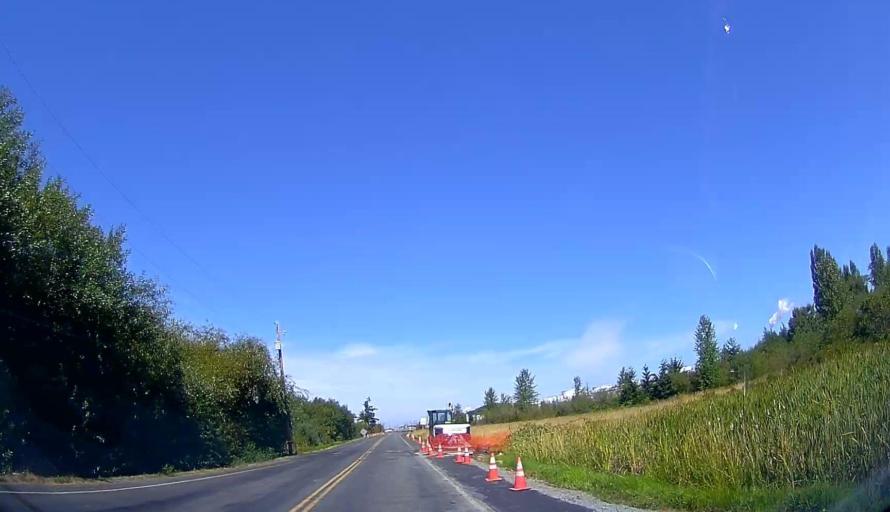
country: US
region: Washington
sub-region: Skagit County
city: Anacortes
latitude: 48.4641
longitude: -122.5708
